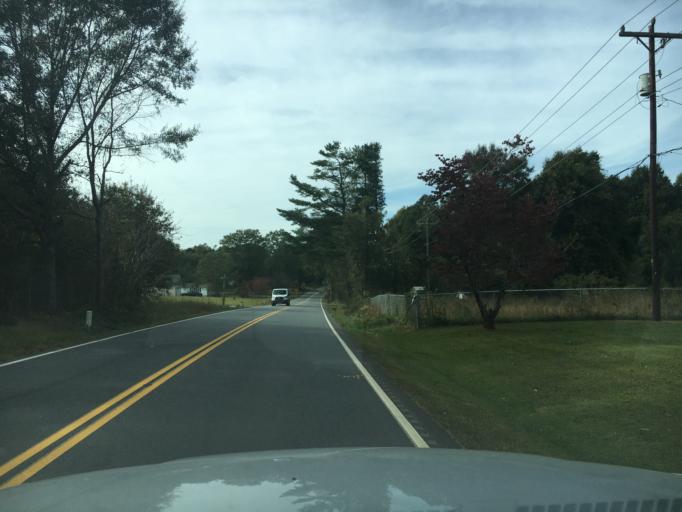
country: US
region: South Carolina
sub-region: Spartanburg County
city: Duncan
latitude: 34.8895
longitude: -82.1368
